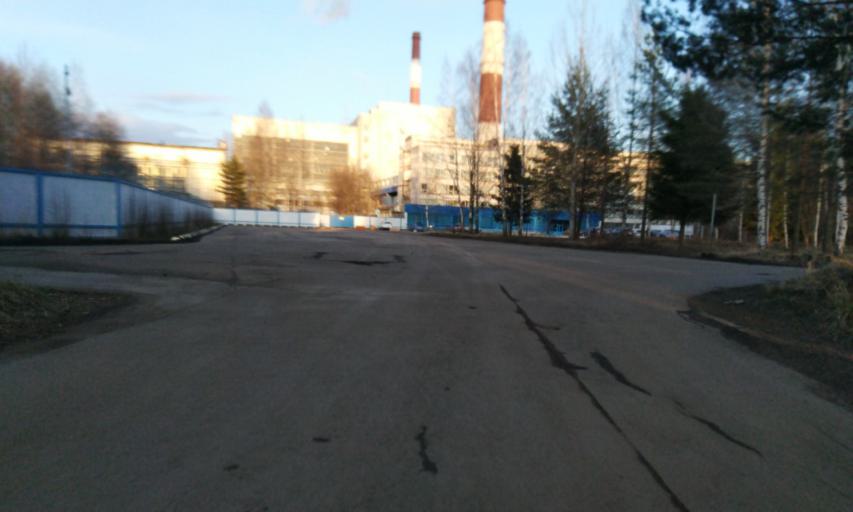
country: RU
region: Leningrad
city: Novoye Devyatkino
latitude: 60.0765
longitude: 30.4689
